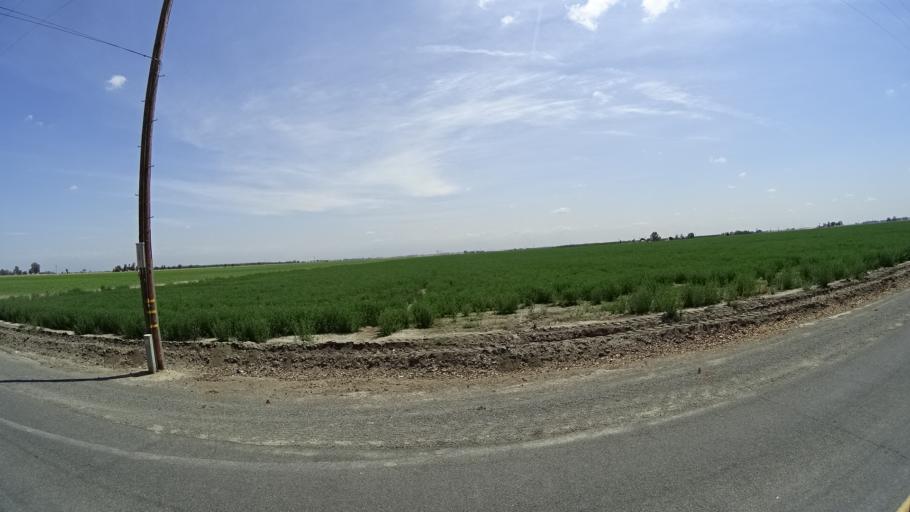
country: US
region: California
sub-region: Tulare County
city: Goshen
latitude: 36.3203
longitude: -119.4753
